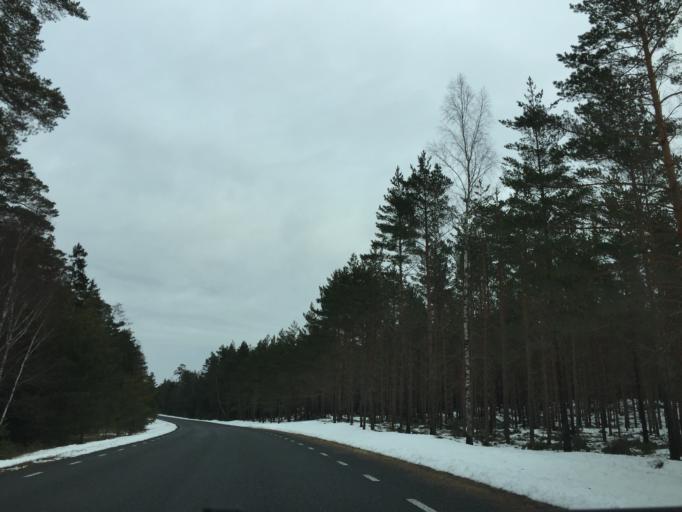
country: EE
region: Saare
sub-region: Kuressaare linn
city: Kuressaare
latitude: 58.4323
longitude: 22.2105
